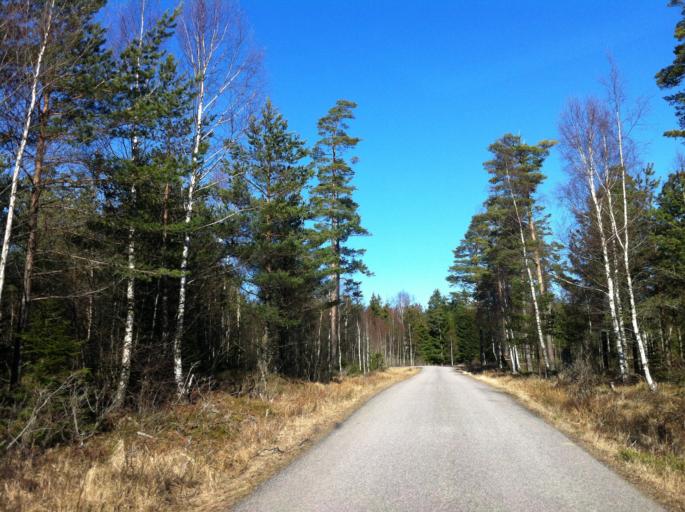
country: SE
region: Vaestra Goetaland
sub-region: Vanersborgs Kommun
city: Vargon
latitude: 58.3559
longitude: 12.4107
